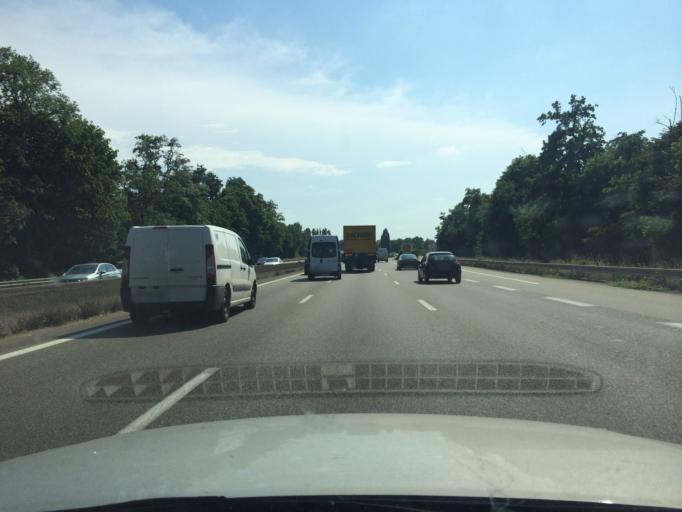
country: FR
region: Alsace
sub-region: Departement du Bas-Rhin
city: Ostwald
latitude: 48.5406
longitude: 7.7207
